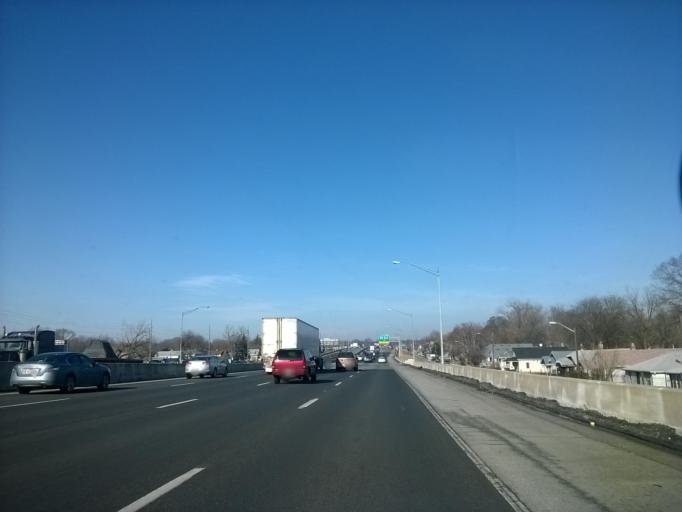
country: US
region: Indiana
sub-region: Marion County
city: Indianapolis
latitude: 39.8000
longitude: -86.1657
